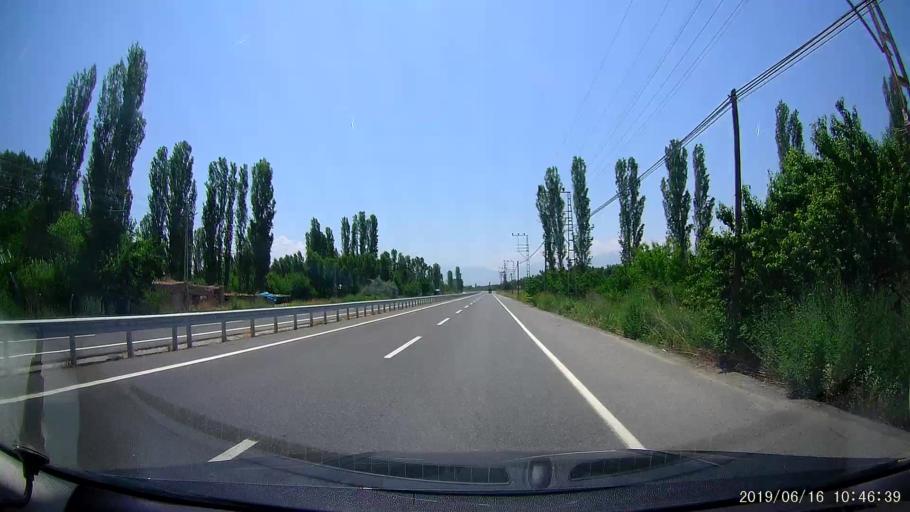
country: AM
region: Armavir
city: Shenavan
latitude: 40.0197
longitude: 43.8806
